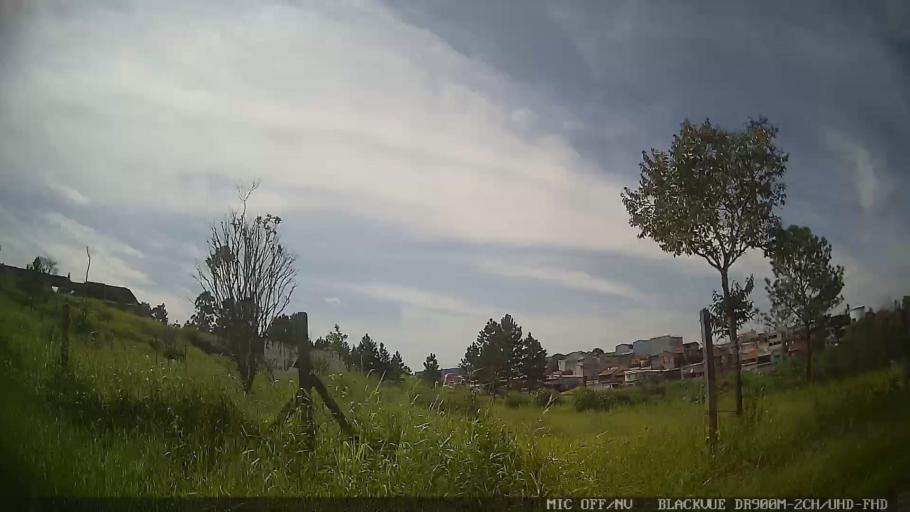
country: BR
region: Sao Paulo
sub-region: Suzano
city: Suzano
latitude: -23.4939
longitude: -46.2917
